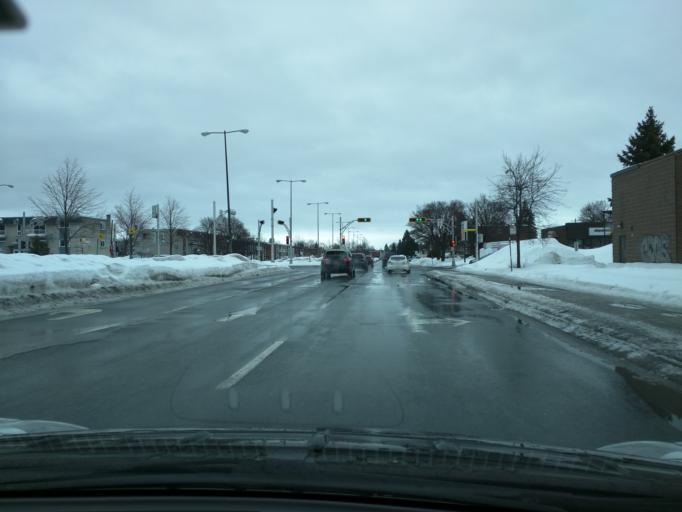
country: CA
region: Quebec
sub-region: Monteregie
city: Longueuil
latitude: 45.5151
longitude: -73.4663
